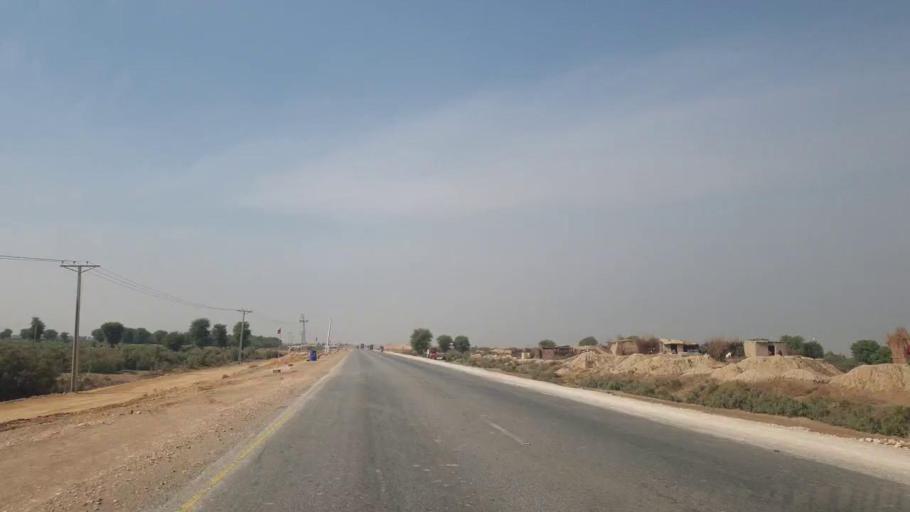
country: PK
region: Sindh
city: Sann
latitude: 26.0020
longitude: 68.1604
